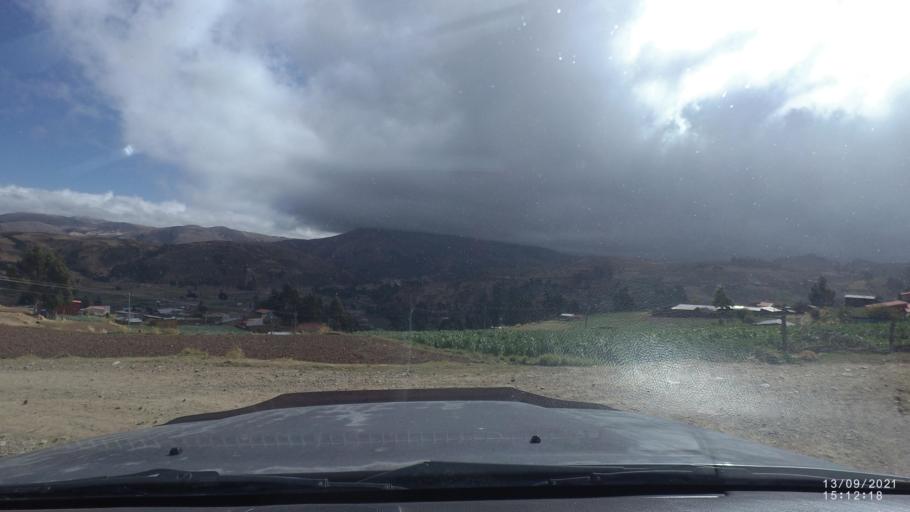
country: BO
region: Cochabamba
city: Colomi
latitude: -17.3613
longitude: -65.8064
